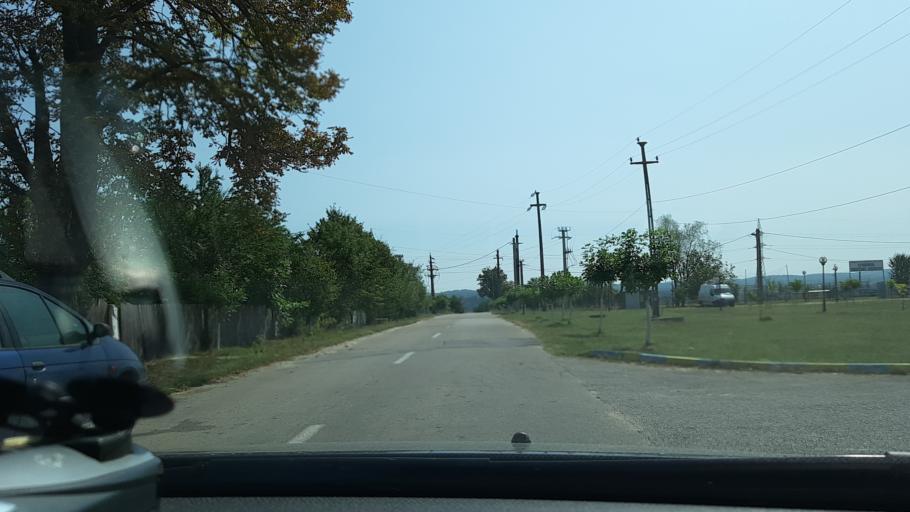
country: RO
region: Gorj
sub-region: Comuna Targu Carbunesti
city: Targu Carbunesti
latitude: 44.9641
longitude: 23.5162
